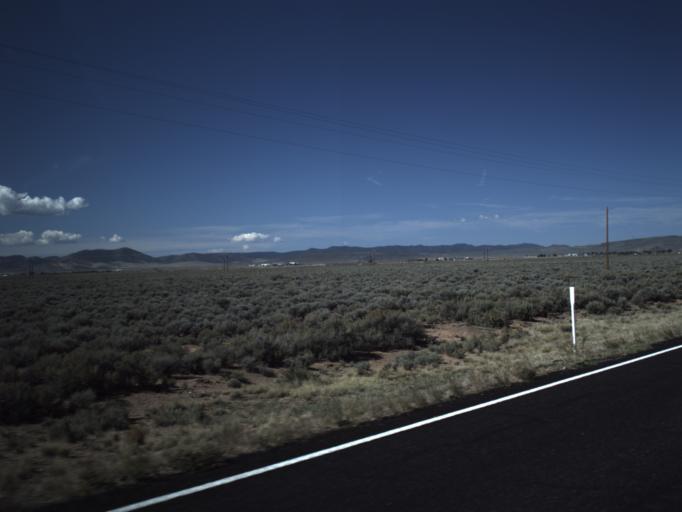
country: US
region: Utah
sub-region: Washington County
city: Enterprise
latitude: 37.6902
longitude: -113.6025
